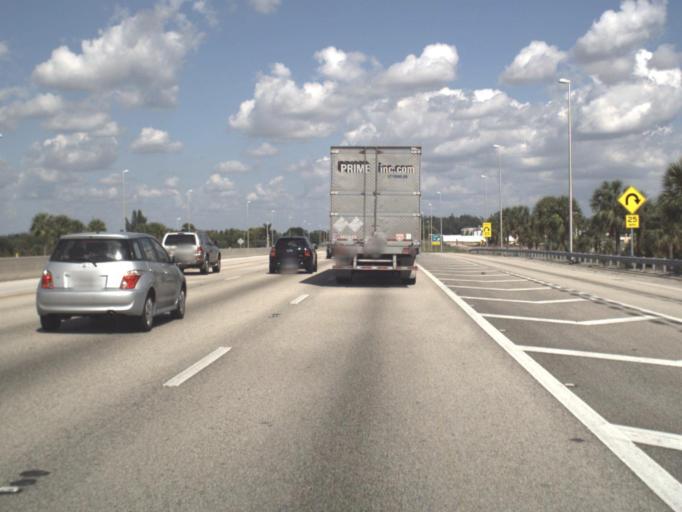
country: US
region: Florida
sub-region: Palm Beach County
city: Villages of Oriole
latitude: 26.4549
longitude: -80.1744
